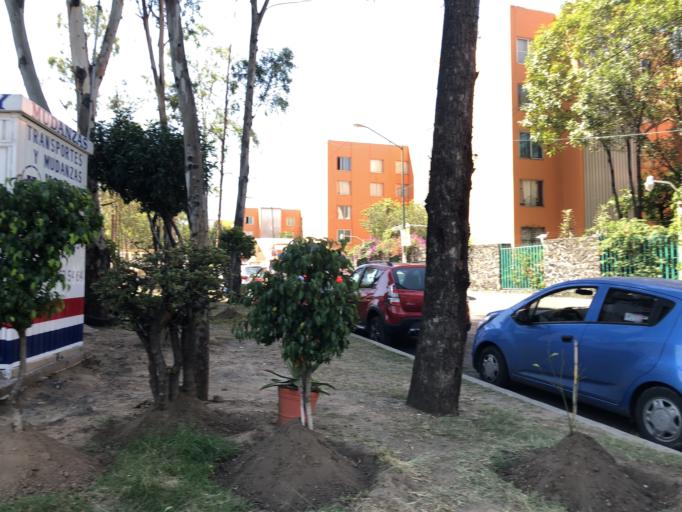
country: MX
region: Mexico City
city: Tlalpan
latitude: 19.3024
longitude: -99.1677
